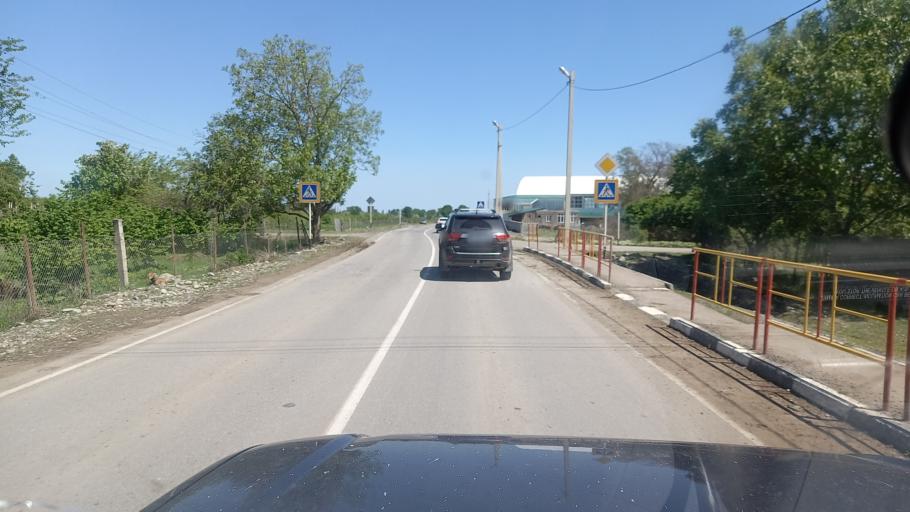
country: RU
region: Dagestan
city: Samur
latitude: 41.7640
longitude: 48.4904
